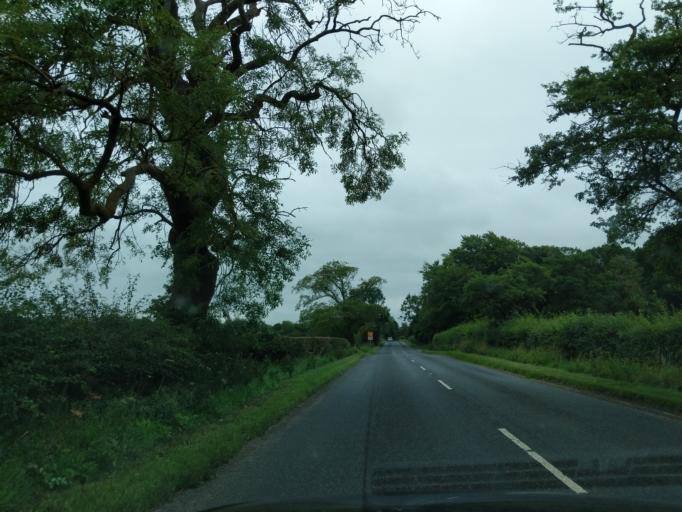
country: GB
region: Scotland
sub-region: East Lothian
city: Ormiston
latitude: 55.9074
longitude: -2.9281
